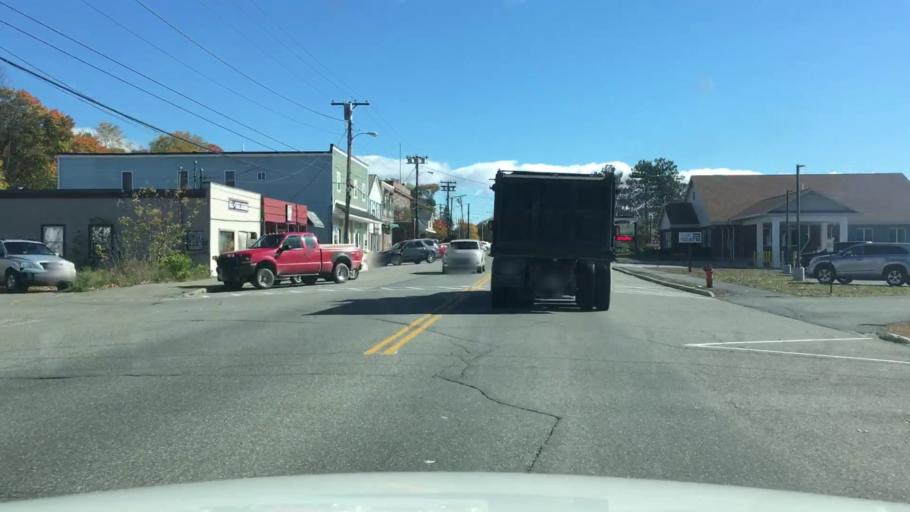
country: US
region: Maine
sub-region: Penobscot County
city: East Millinocket
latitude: 45.6259
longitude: -68.5771
